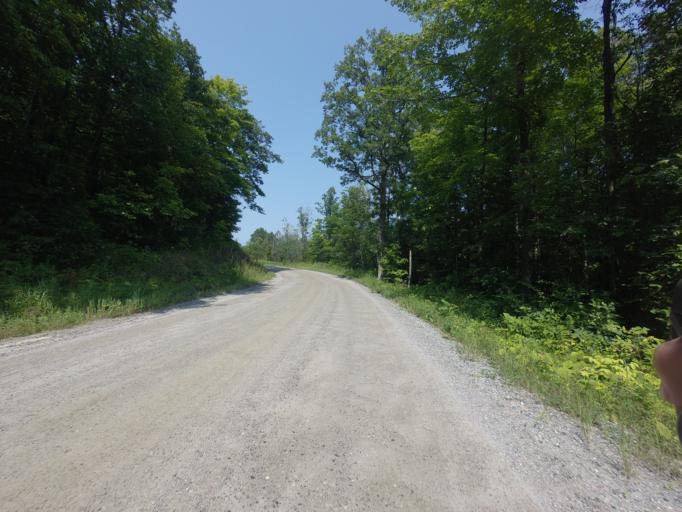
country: CA
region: Ontario
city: Kingston
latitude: 44.6540
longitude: -76.6849
